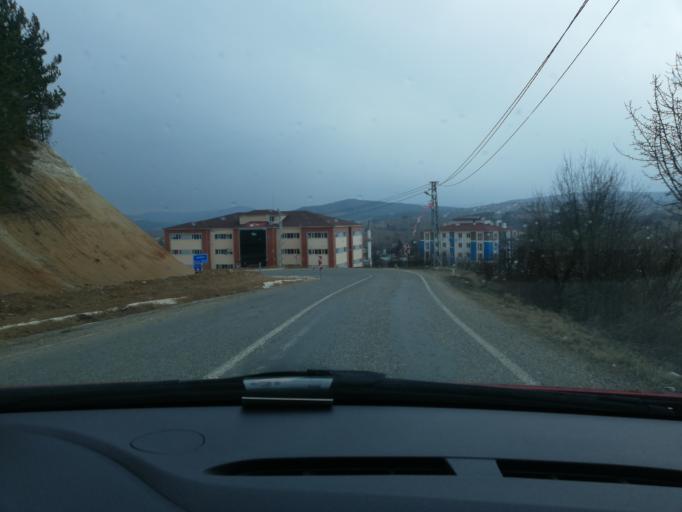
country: TR
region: Kastamonu
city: Daday
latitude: 41.4825
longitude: 33.4603
